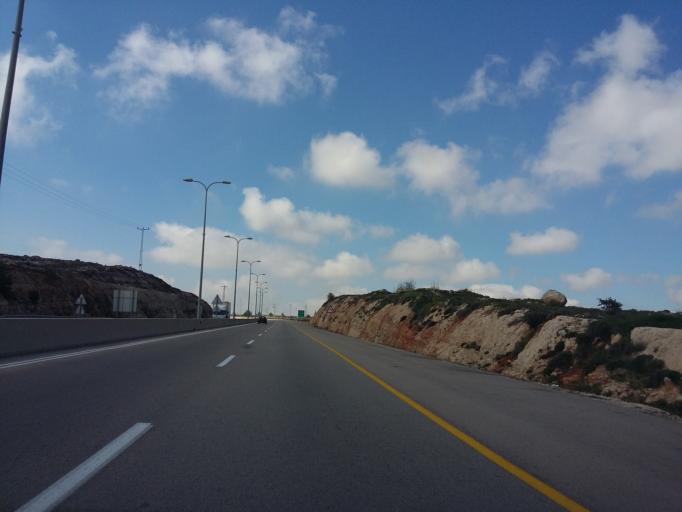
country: IL
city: Givat Zeev
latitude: 31.8699
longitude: 35.1763
